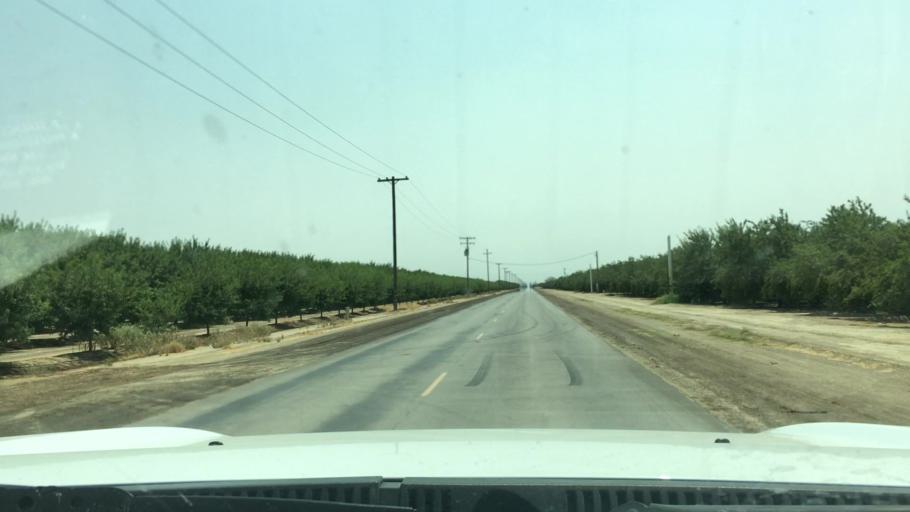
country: US
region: California
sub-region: Kern County
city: Wasco
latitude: 35.6416
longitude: -119.4376
